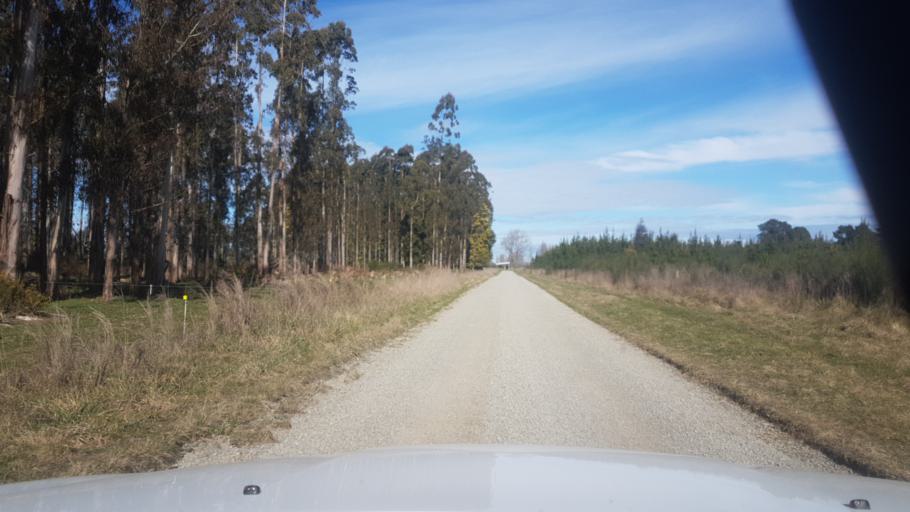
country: NZ
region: Canterbury
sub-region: Timaru District
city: Pleasant Point
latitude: -44.1410
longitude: 171.2753
